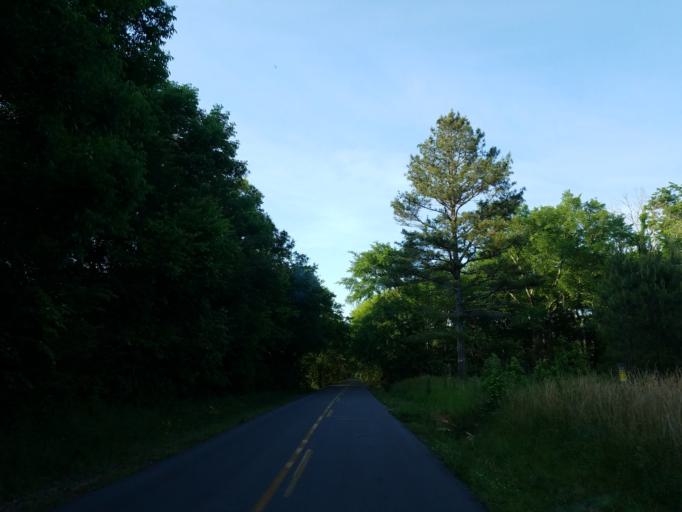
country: US
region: Georgia
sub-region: Gordon County
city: Calhoun
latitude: 34.5299
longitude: -85.1114
